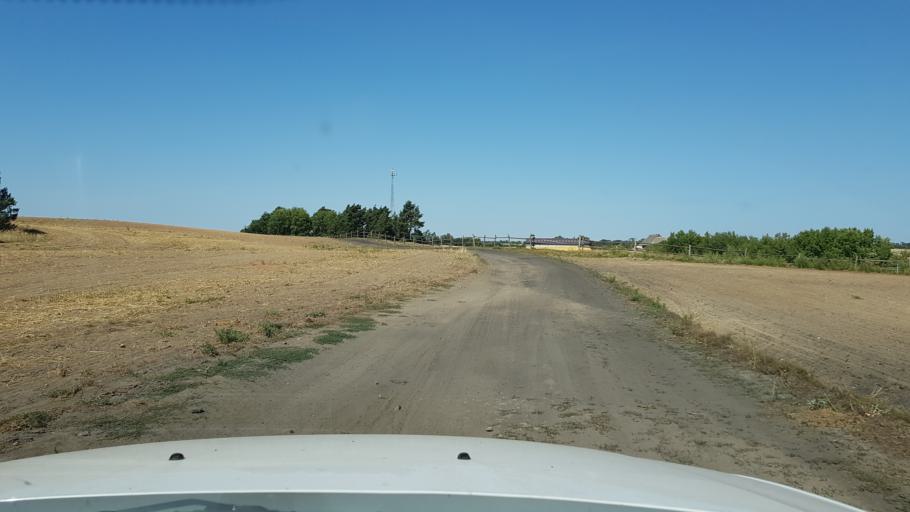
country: PL
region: West Pomeranian Voivodeship
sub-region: Powiat gryfinski
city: Moryn
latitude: 52.8529
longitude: 14.3588
